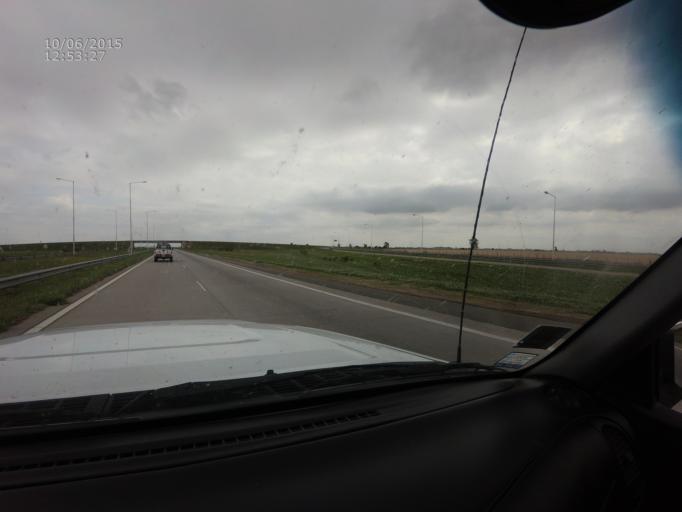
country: AR
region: Santa Fe
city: Armstrong
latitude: -32.8190
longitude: -61.5513
